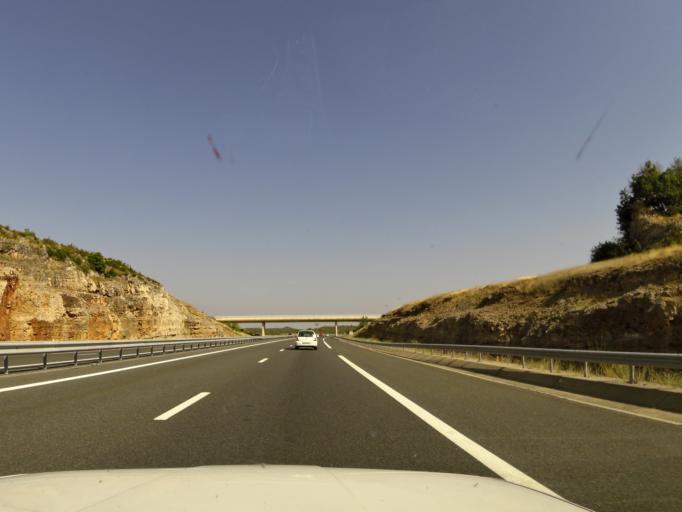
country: FR
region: Midi-Pyrenees
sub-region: Departement de l'Aveyron
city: Creissels
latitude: 44.0535
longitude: 3.0447
